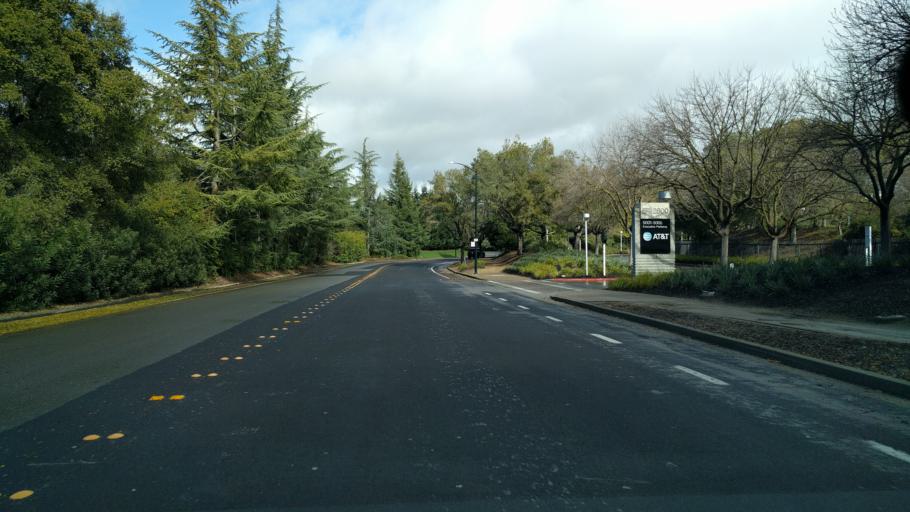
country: US
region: California
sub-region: Contra Costa County
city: San Ramon
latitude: 37.7656
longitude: -121.9684
